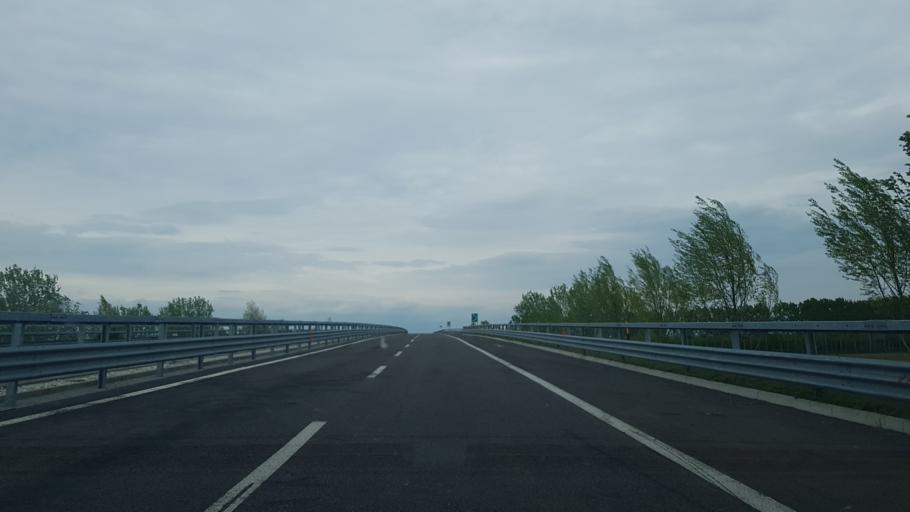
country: IT
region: Veneto
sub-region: Provincia di Padova
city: Piacenza d'Adige
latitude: 45.1514
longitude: 11.5328
